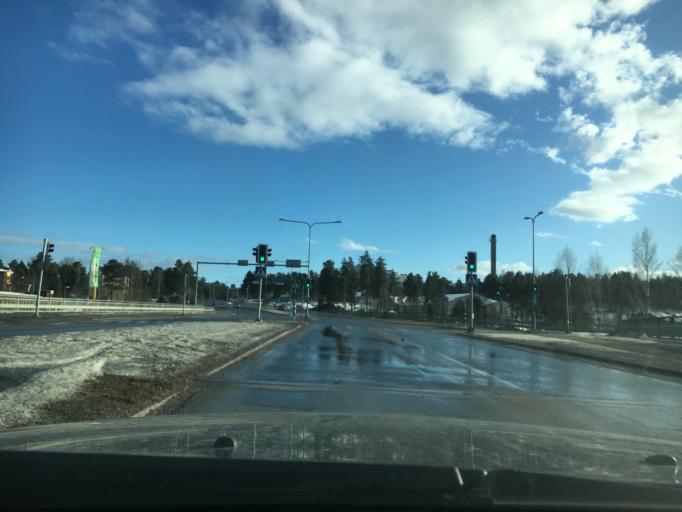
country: FI
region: Kainuu
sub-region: Kajaani
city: Kajaani
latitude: 64.2195
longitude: 27.7292
